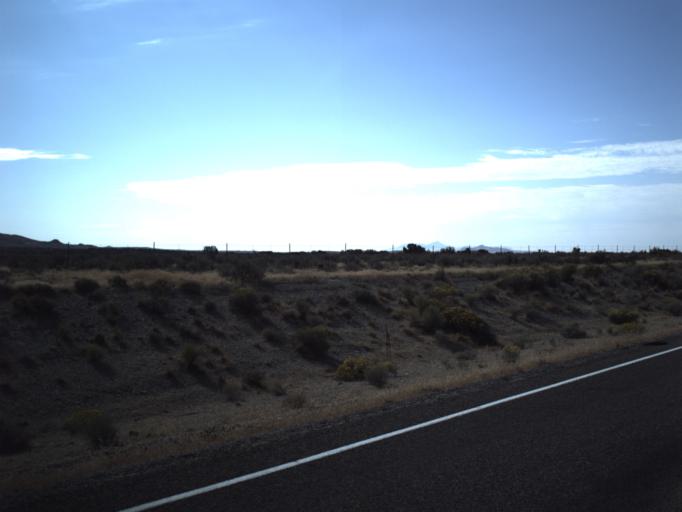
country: US
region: Idaho
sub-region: Cassia County
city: Burley
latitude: 41.6578
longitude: -113.5489
